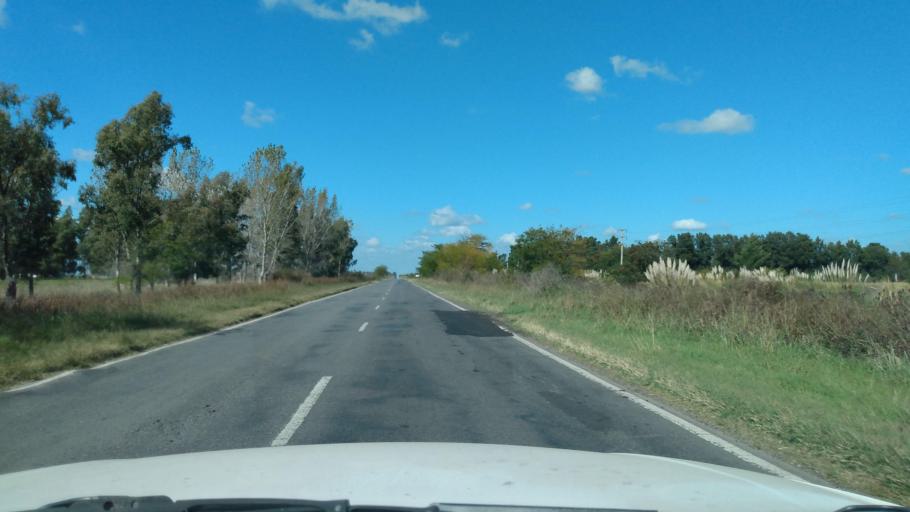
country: AR
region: Buenos Aires
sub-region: Partido de Mercedes
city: Mercedes
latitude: -34.7175
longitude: -59.3961
